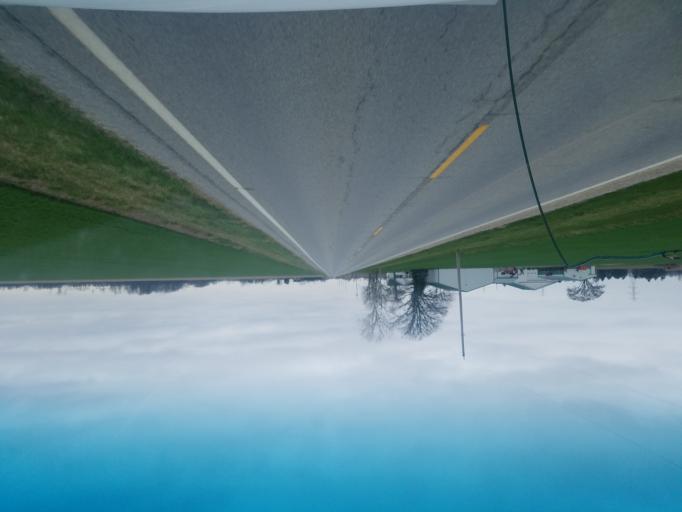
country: US
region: Ohio
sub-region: Allen County
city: Delphos
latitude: 40.9321
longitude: -84.4282
